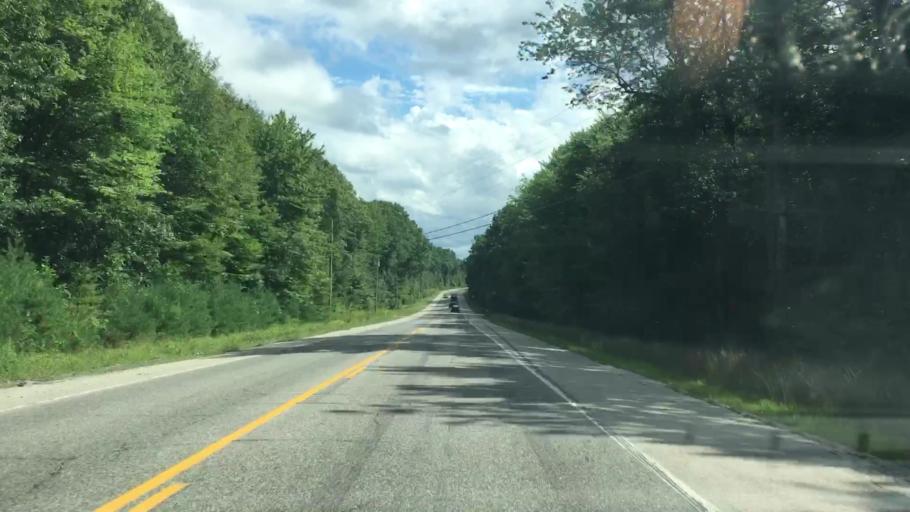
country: US
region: Maine
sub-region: York County
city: South Sanford
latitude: 43.3647
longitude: -70.7311
